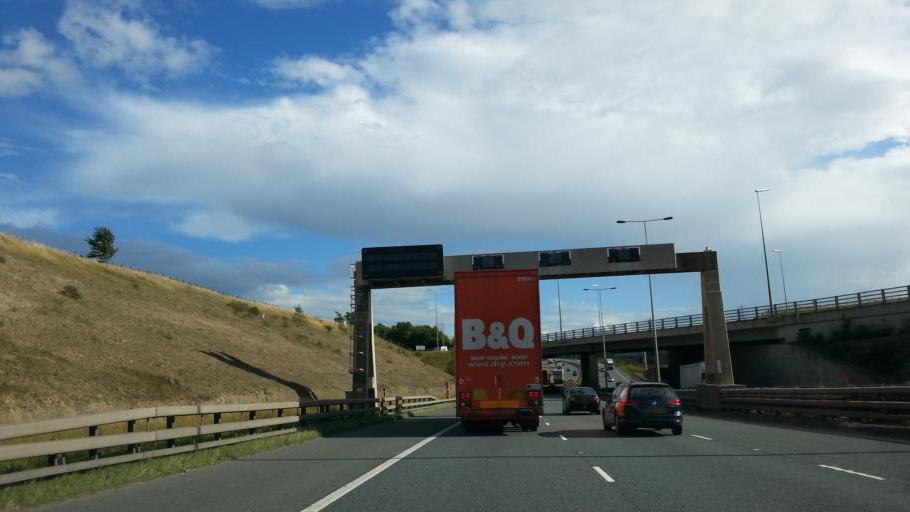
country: GB
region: England
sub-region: City and Borough of Wakefield
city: Ferrybridge
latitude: 53.7005
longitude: -1.2758
